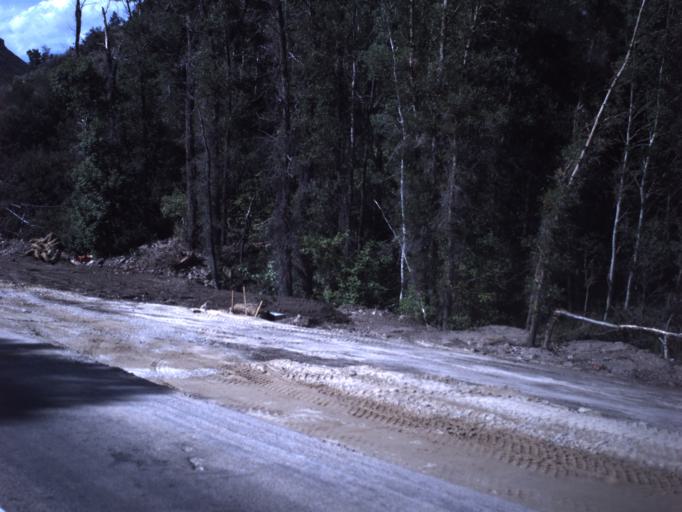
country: US
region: Utah
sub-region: Wasatch County
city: Heber
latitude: 40.3812
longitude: -111.2995
